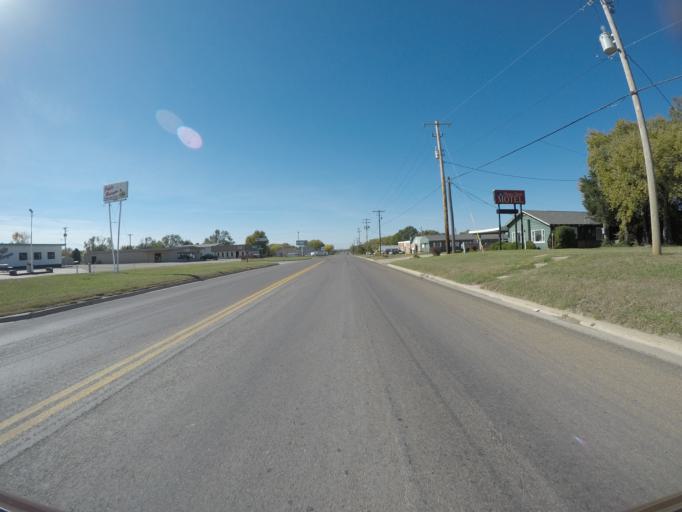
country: US
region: Kansas
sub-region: Smith County
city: Smith Center
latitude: 39.7852
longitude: -98.7748
